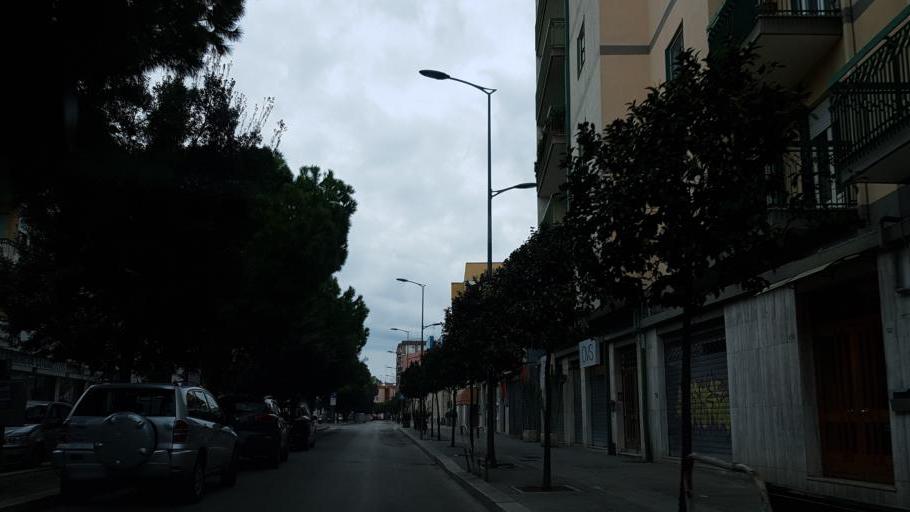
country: IT
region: Apulia
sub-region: Provincia di Brindisi
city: Brindisi
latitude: 40.6307
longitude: 17.9350
